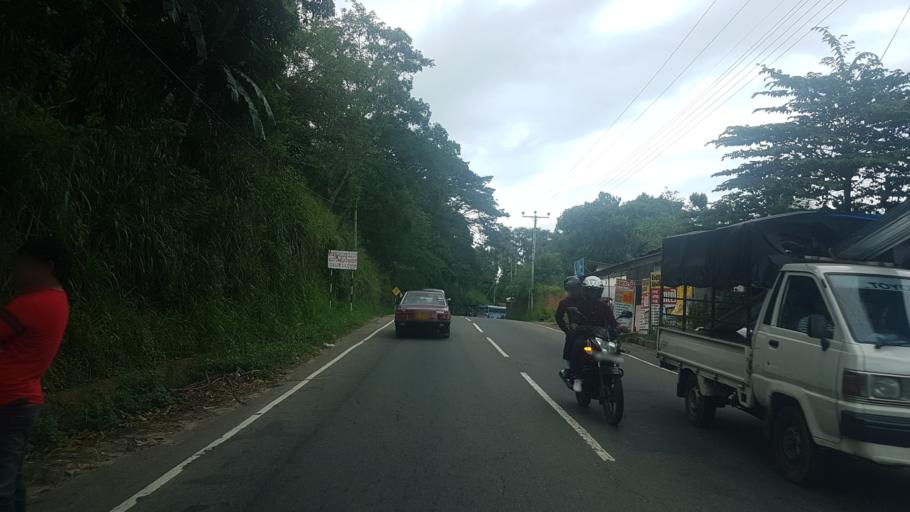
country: LK
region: Central
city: Kandy
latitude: 7.2404
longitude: 80.5933
